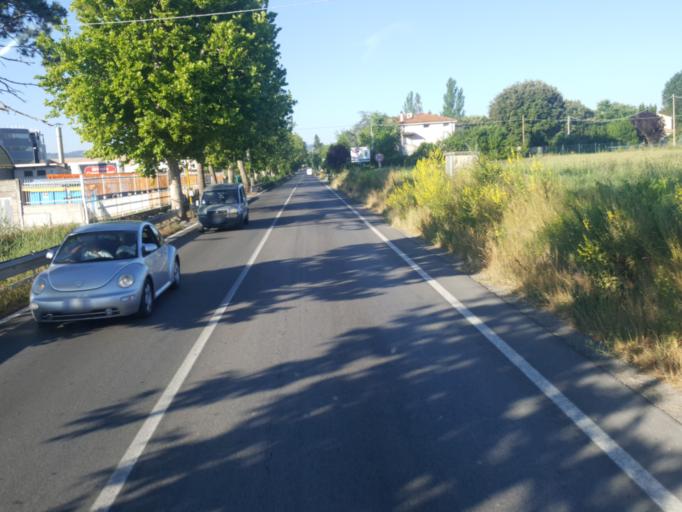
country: IT
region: The Marches
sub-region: Provincia di Pesaro e Urbino
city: Villa Ceccolini
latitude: 43.8886
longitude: 12.8316
